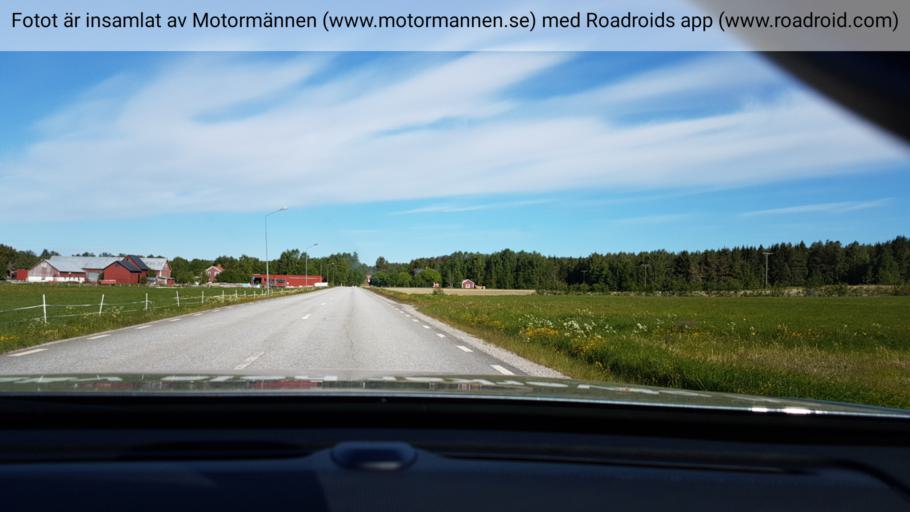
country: SE
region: Vaesterbotten
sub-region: Vindelns Kommun
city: Vindeln
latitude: 64.1238
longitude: 19.5577
